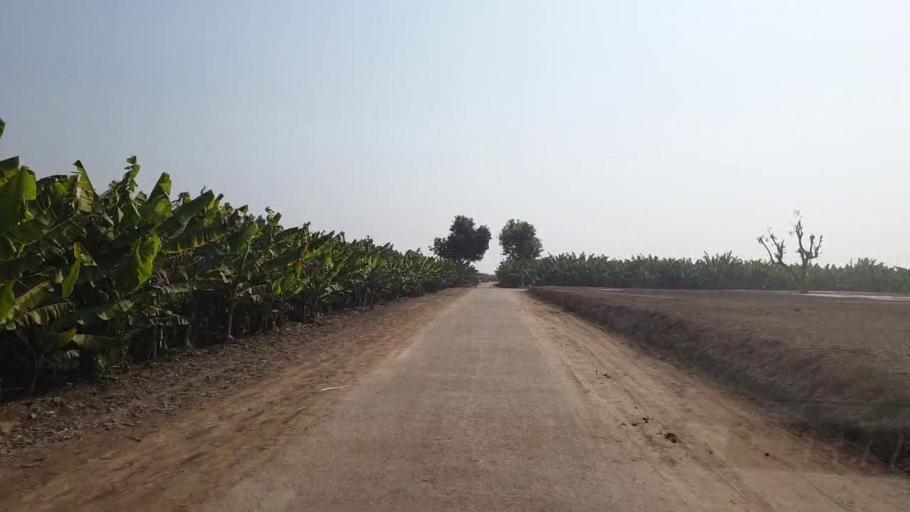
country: PK
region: Sindh
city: Bhit Shah
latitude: 25.7901
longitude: 68.4988
